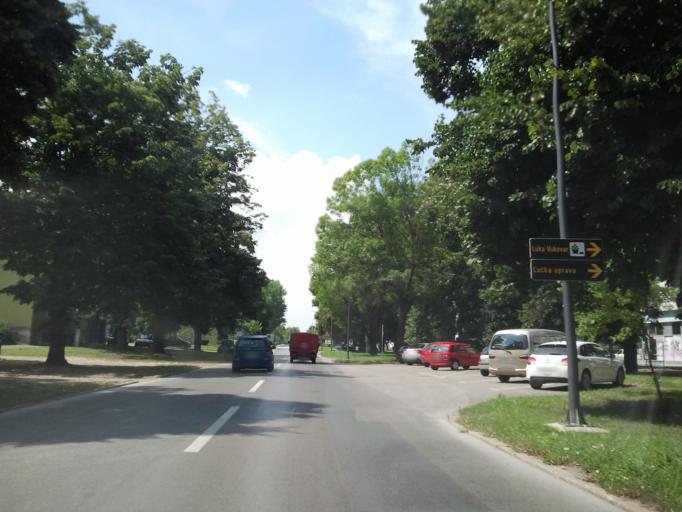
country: HR
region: Vukovarsko-Srijemska
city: Vukovar
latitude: 45.3591
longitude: 18.9923
